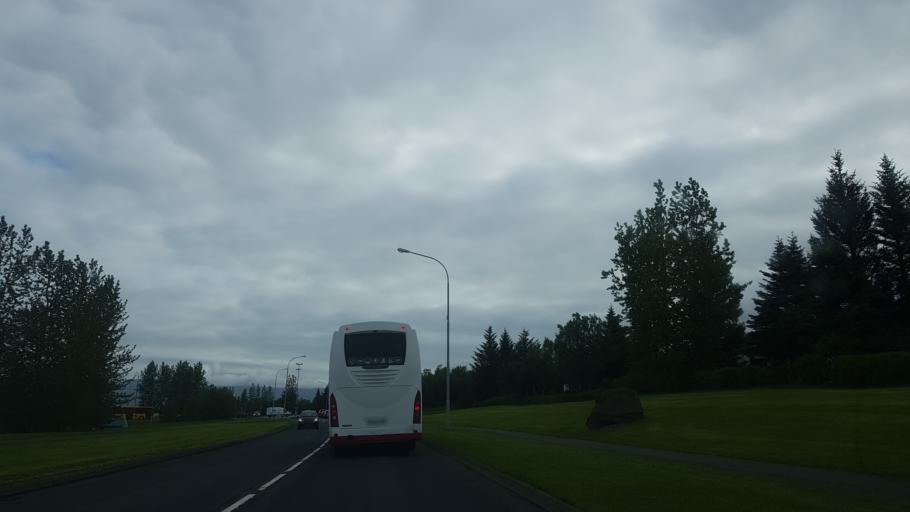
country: IS
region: Capital Region
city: Reykjavik
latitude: 64.1047
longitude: -21.8438
